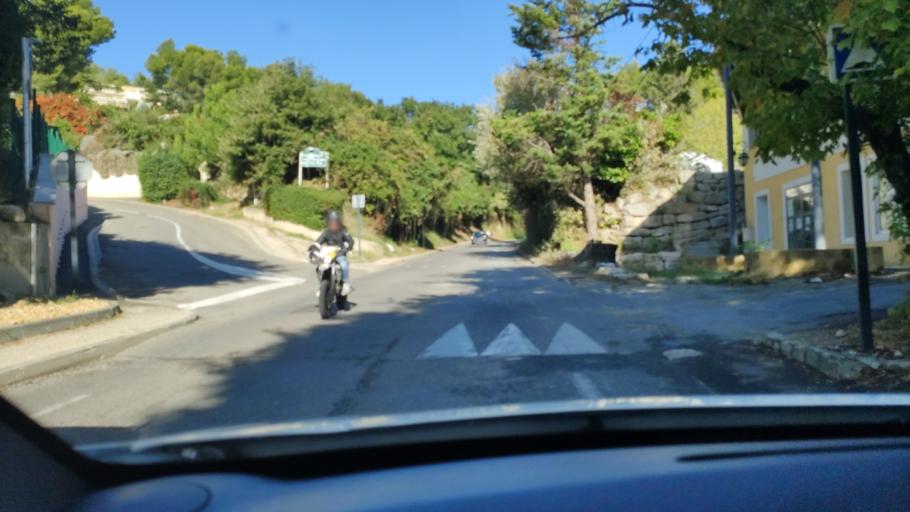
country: FR
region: Languedoc-Roussillon
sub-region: Departement du Gard
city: Villeneuve-les-Avignon
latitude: 43.9725
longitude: 4.7911
